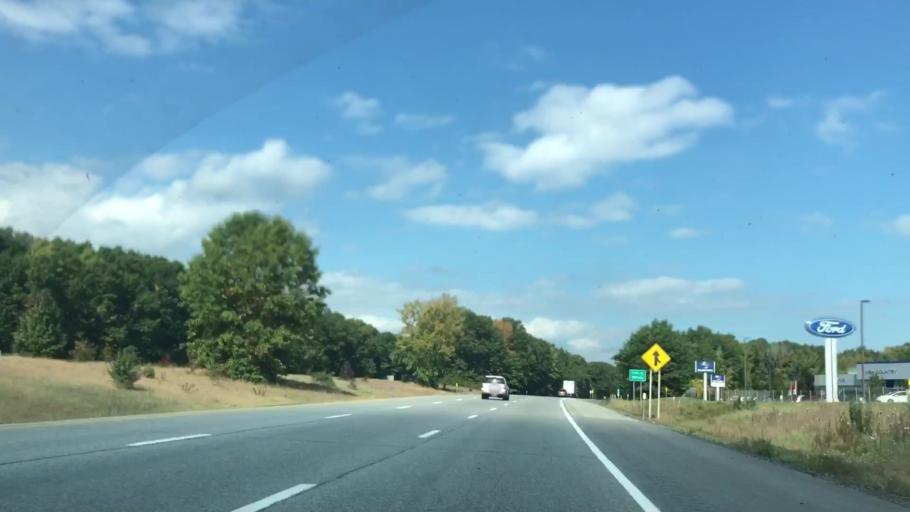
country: US
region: New York
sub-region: Saratoga County
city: Saratoga Springs
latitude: 43.0978
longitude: -73.7523
